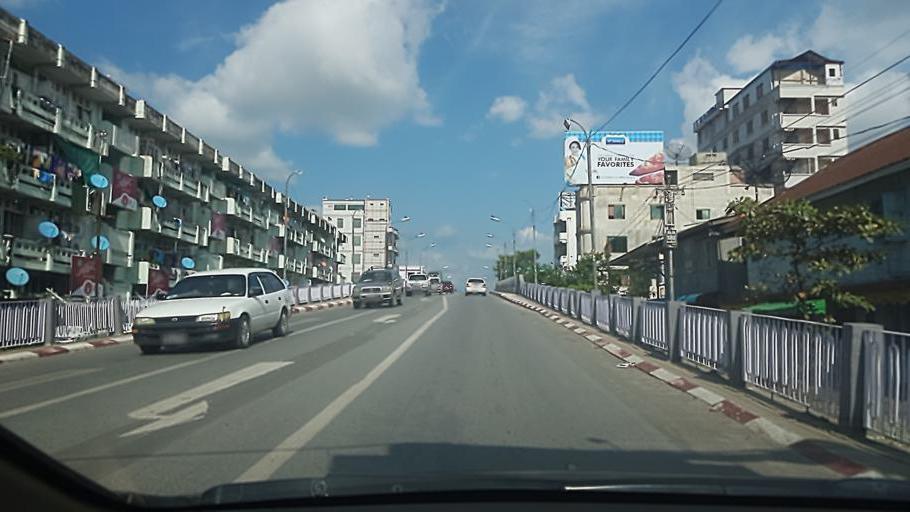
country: MM
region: Mandalay
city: Mandalay
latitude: 21.9693
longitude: 96.0837
